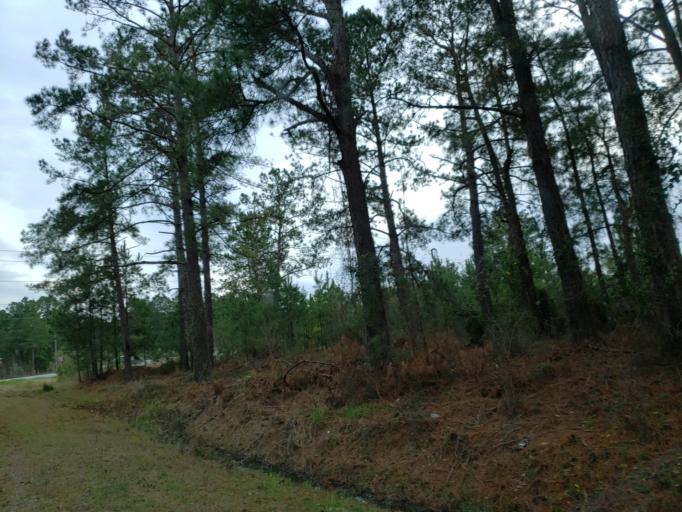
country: US
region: Georgia
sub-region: Crisp County
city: Cordele
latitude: 32.0059
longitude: -83.7548
